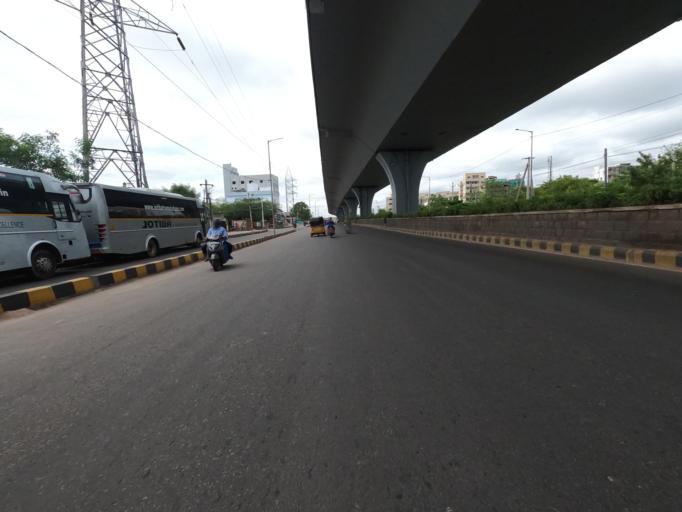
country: IN
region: Telangana
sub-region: Hyderabad
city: Hyderabad
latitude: 17.3392
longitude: 78.4251
